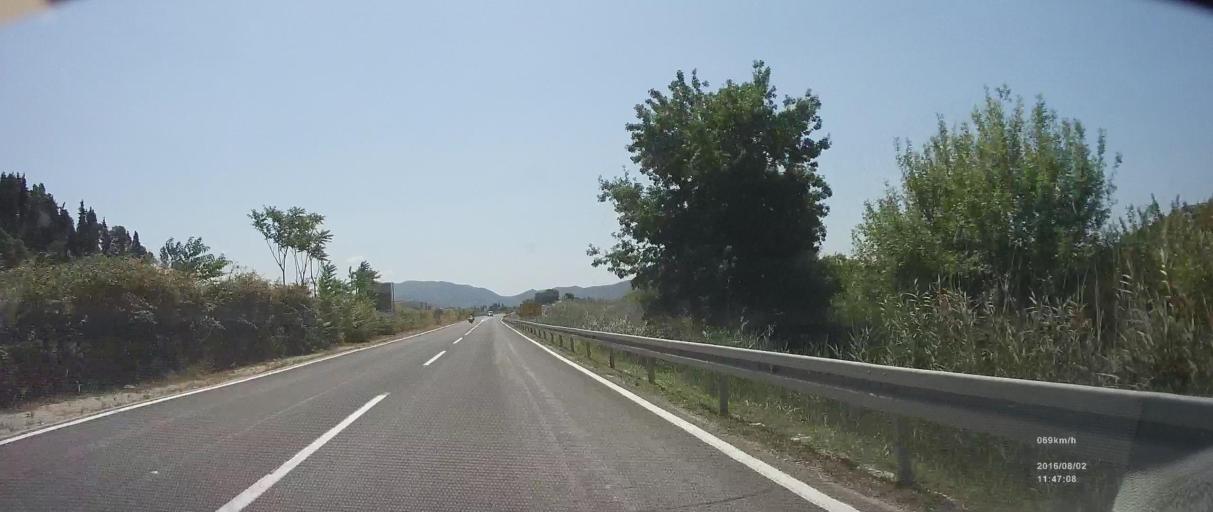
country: HR
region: Dubrovacko-Neretvanska
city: Komin
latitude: 43.0470
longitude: 17.4800
